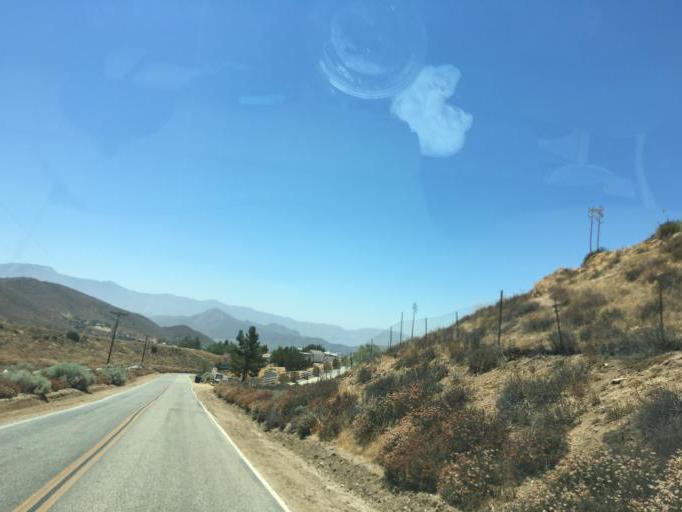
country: US
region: California
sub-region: Los Angeles County
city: Acton
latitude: 34.5226
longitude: -118.2115
